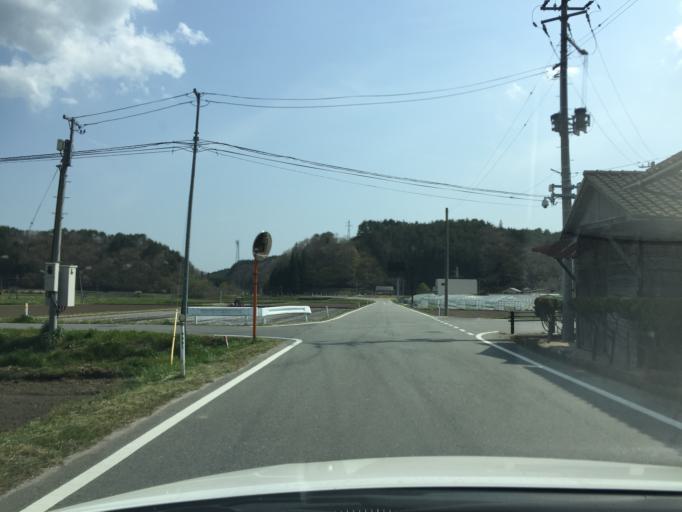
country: JP
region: Fukushima
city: Namie
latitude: 37.3137
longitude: 140.8340
